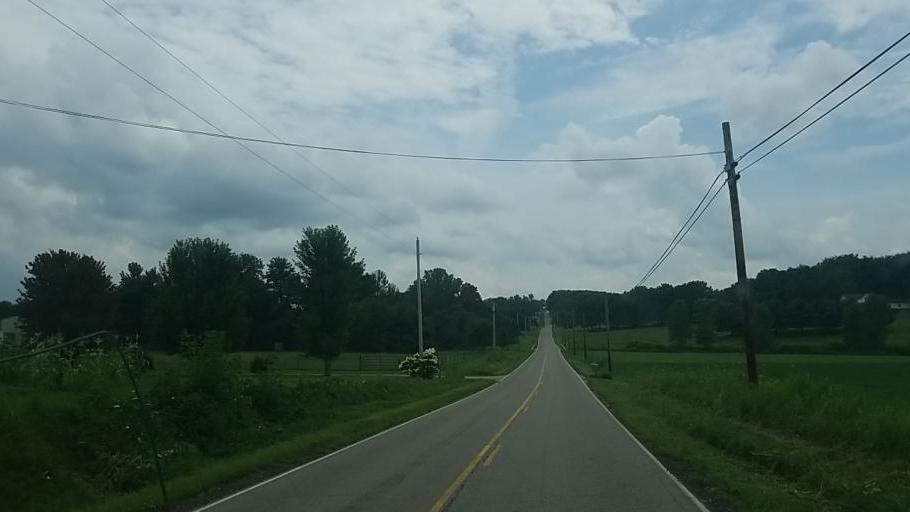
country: US
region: Ohio
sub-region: Licking County
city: Utica
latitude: 40.2279
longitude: -82.3655
